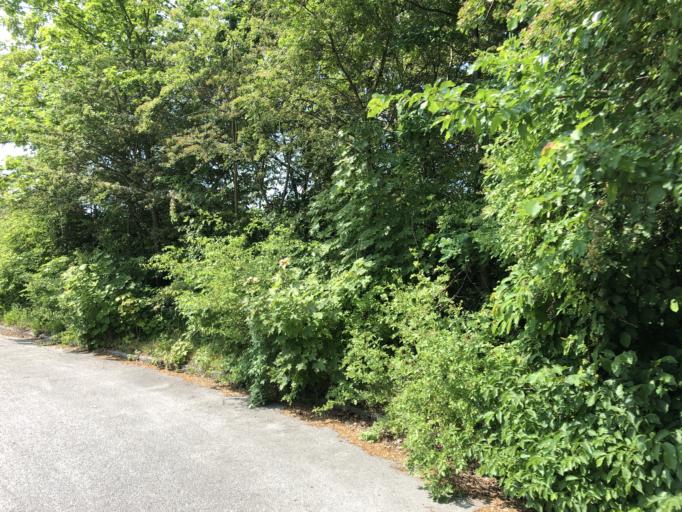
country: SE
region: Skane
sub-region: Lunds Kommun
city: Lund
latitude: 55.7203
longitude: 13.1882
